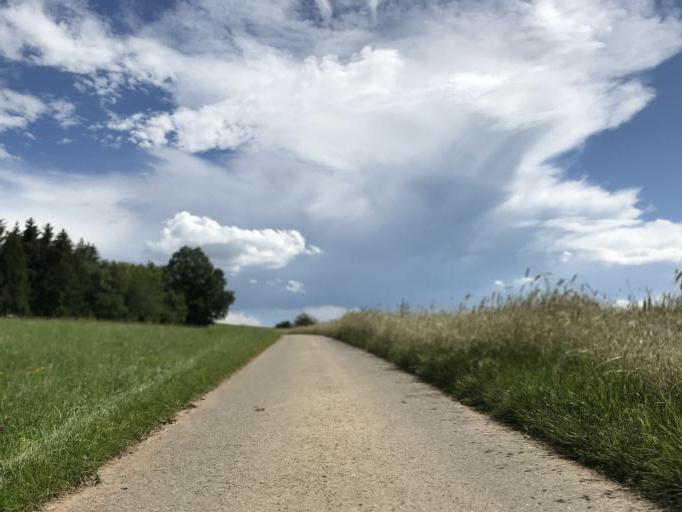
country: DE
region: Baden-Wuerttemberg
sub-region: Freiburg Region
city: Schopfheim
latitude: 47.6373
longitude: 7.8300
